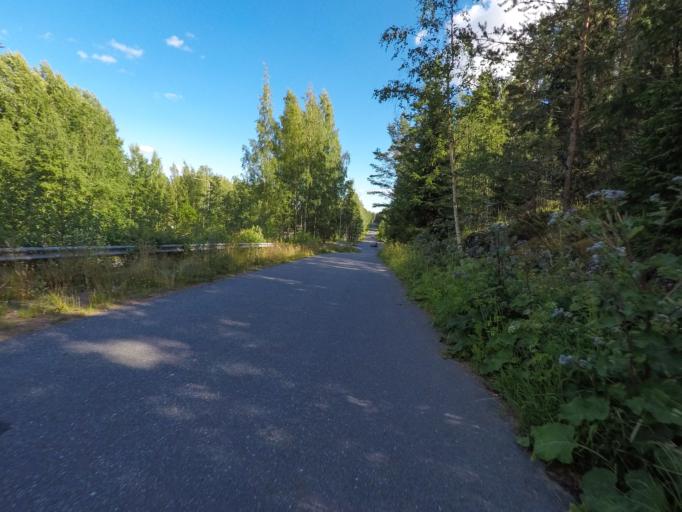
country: FI
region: South Karelia
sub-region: Lappeenranta
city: Lappeenranta
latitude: 61.0898
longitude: 28.1421
